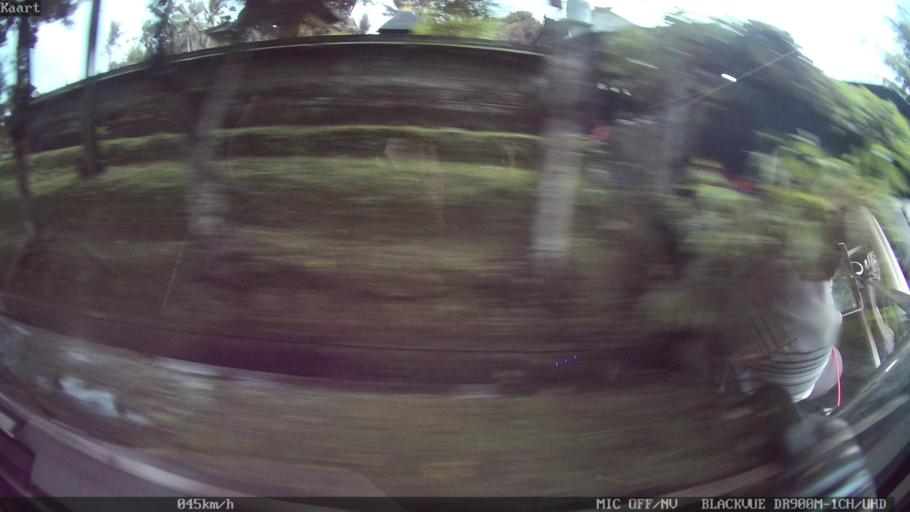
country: ID
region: Bali
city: Banjar Teguan
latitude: -8.5003
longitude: 115.2336
